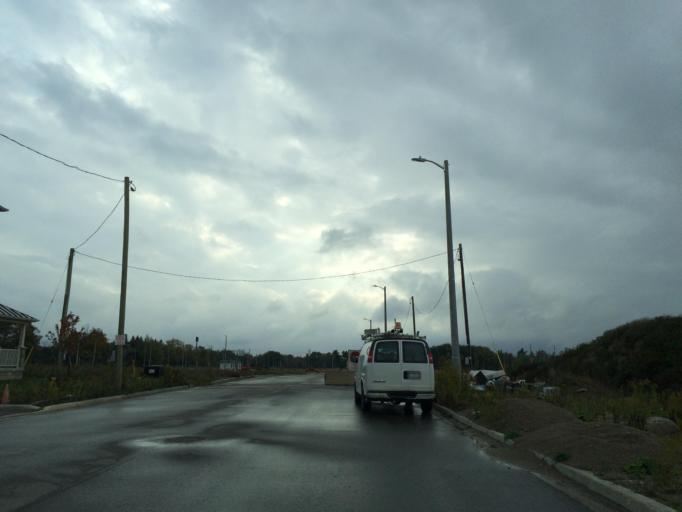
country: CA
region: Ontario
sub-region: Wellington County
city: Guelph
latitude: 43.5252
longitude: -80.1932
